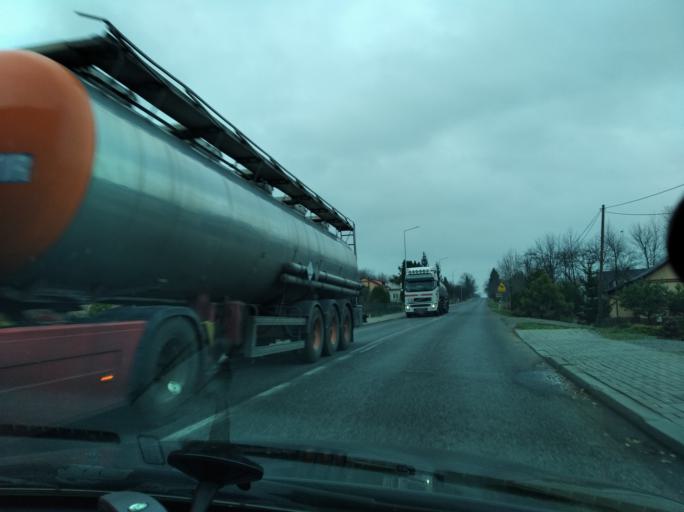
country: PL
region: Subcarpathian Voivodeship
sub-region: Powiat przeworski
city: Sietesz
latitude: 49.9997
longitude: 22.3518
